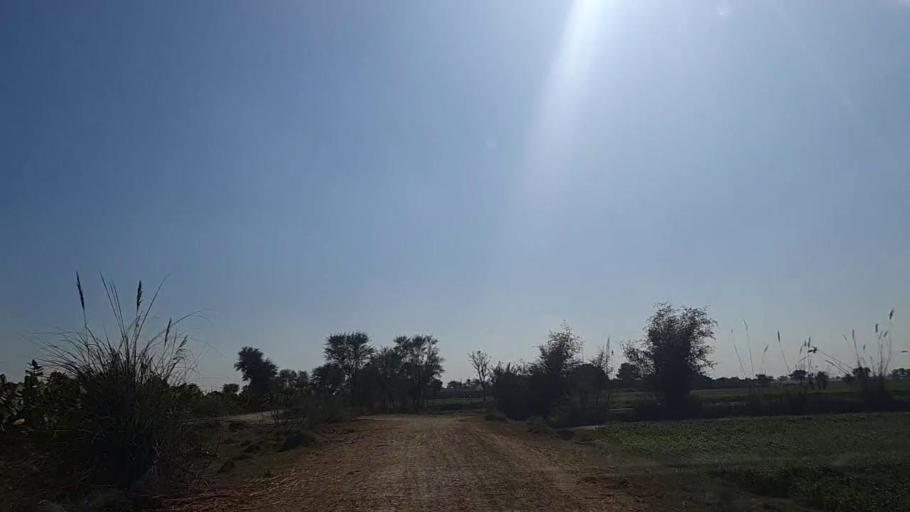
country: PK
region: Sindh
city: Sakrand
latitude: 26.2370
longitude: 68.1997
